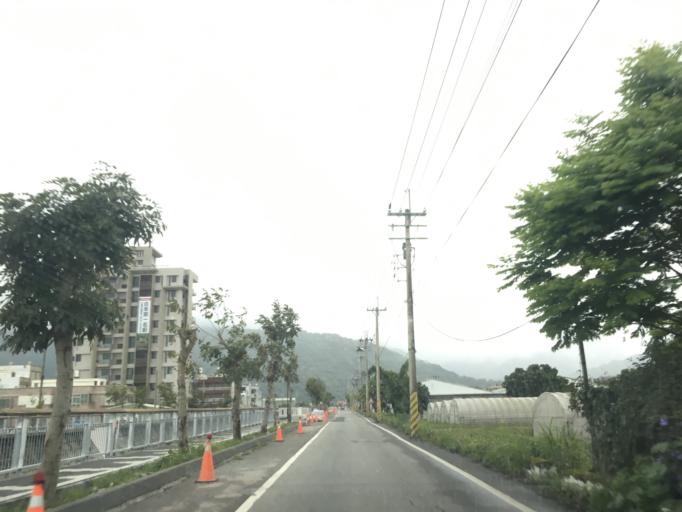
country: TW
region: Taiwan
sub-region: Hualien
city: Hualian
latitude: 23.9839
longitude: 121.5688
